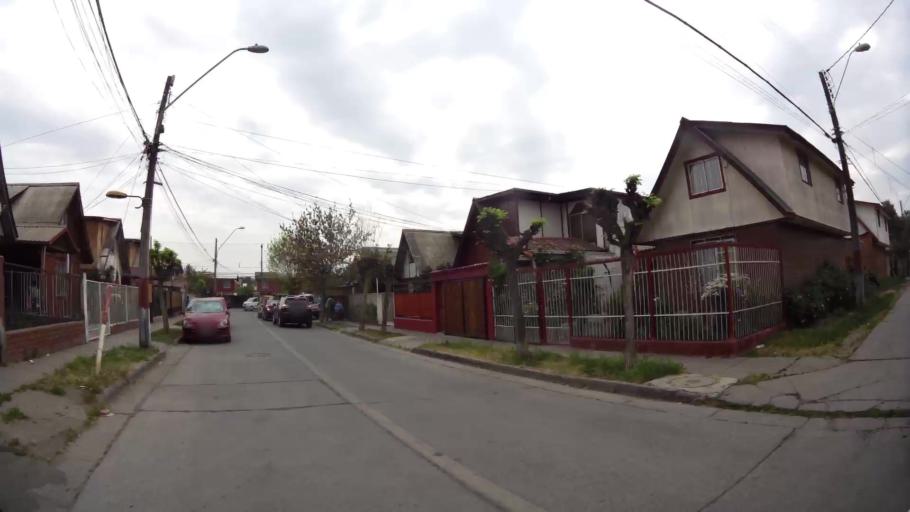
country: CL
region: Santiago Metropolitan
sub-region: Provincia de Santiago
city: Lo Prado
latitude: -33.5009
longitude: -70.7747
